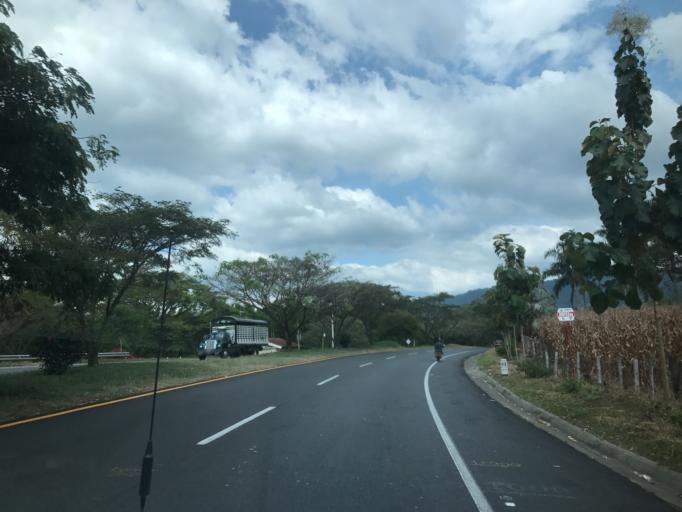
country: CO
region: Valle del Cauca
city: Obando
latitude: 4.6237
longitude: -75.9401
